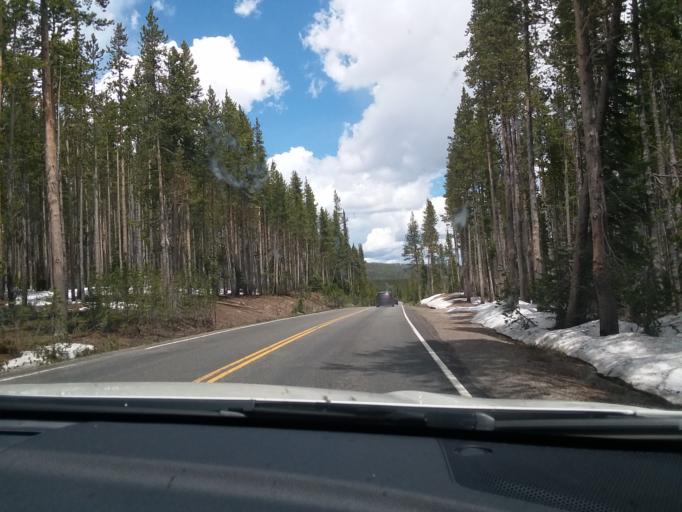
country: US
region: Montana
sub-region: Gallatin County
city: West Yellowstone
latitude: 44.2010
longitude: -110.6600
